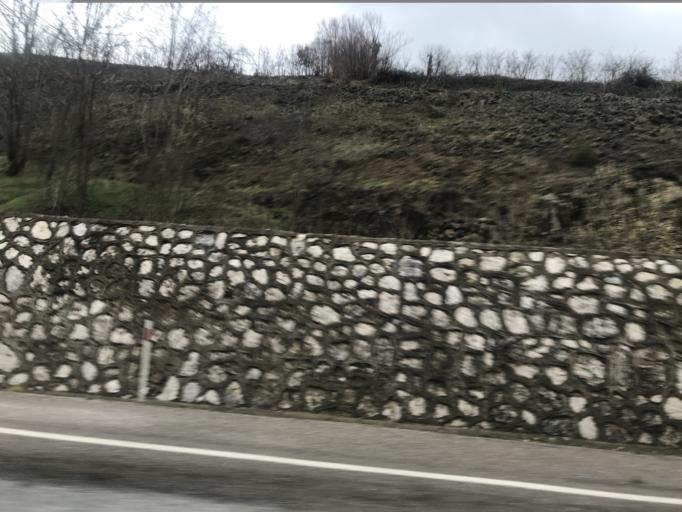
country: TR
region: Bartin
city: Amasra
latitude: 41.7066
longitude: 32.3885
